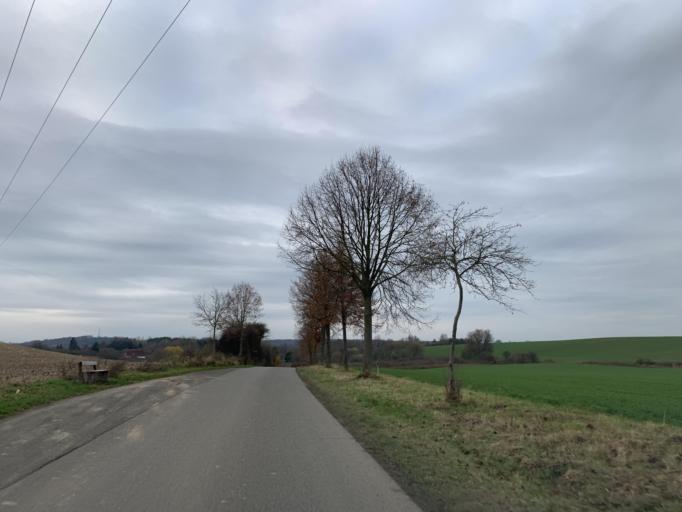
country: DE
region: Mecklenburg-Vorpommern
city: Carpin
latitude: 53.3999
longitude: 13.2074
